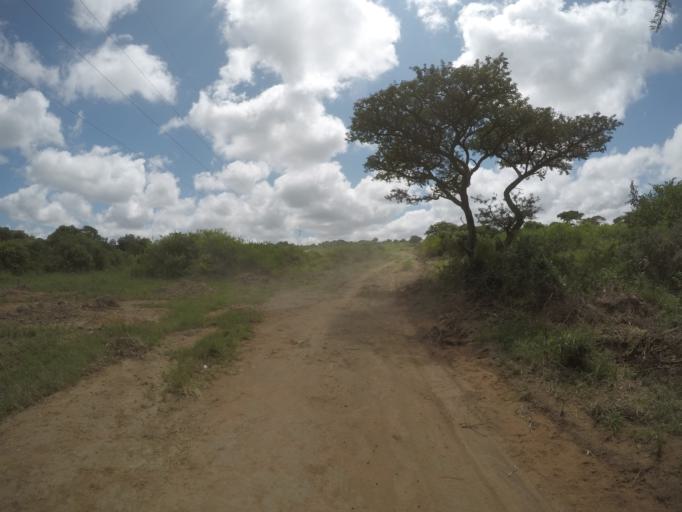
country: ZA
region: KwaZulu-Natal
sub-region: uThungulu District Municipality
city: Empangeni
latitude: -28.5883
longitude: 31.8375
